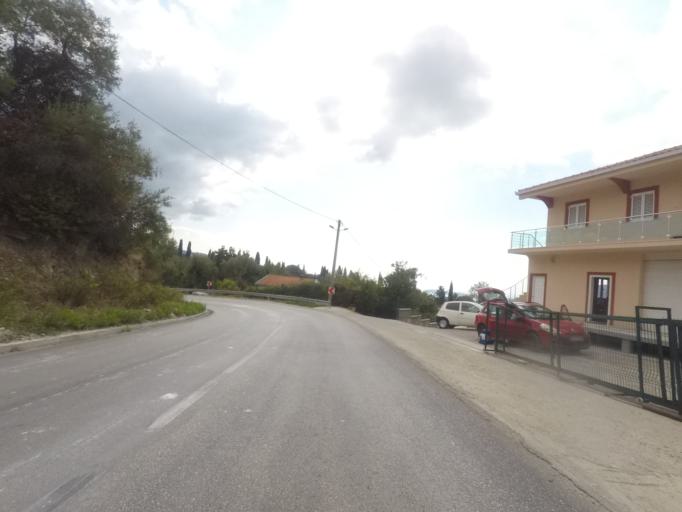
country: ME
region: Herceg Novi
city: Herceg-Novi
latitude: 42.4638
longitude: 18.5457
